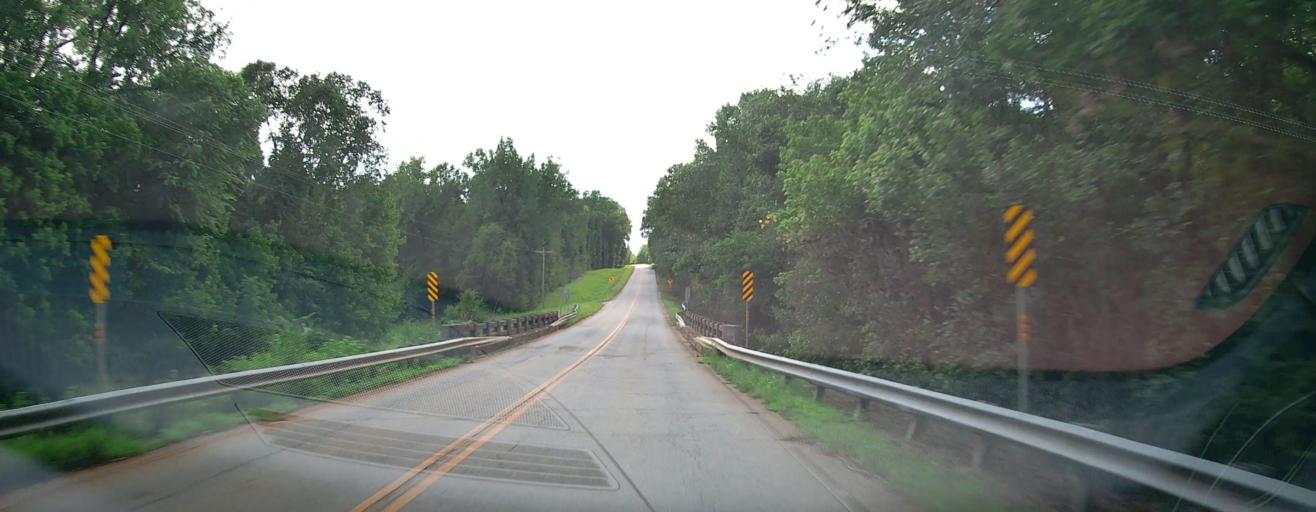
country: US
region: Georgia
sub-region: Crawford County
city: Knoxville
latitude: 32.8807
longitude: -84.0269
